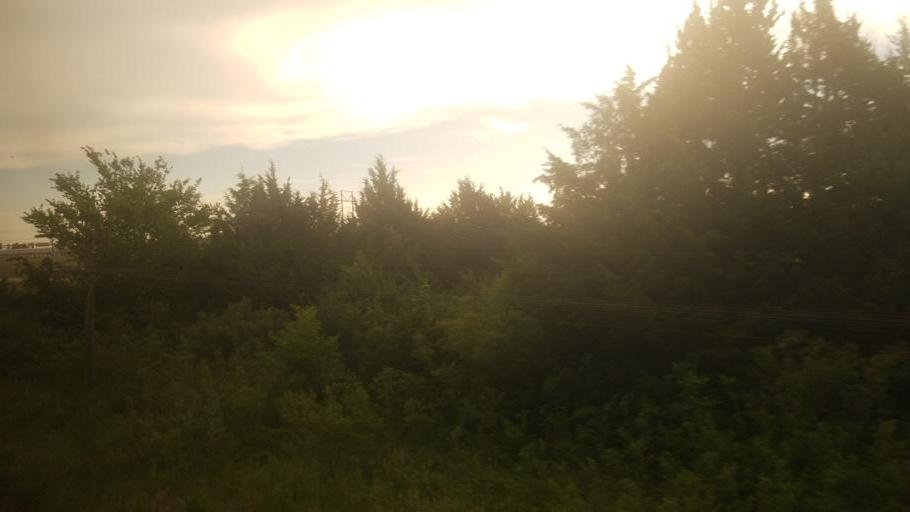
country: US
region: Kansas
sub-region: Osage County
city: Carbondale
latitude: 38.9337
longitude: -95.6888
